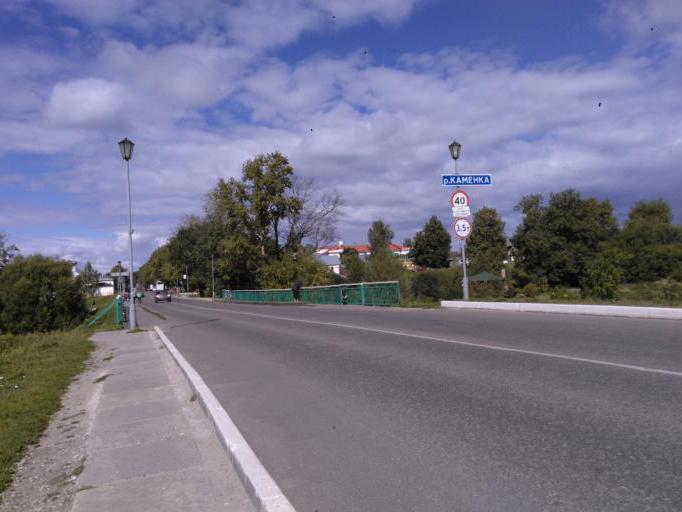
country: RU
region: Vladimir
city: Suzdal'
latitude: 56.4137
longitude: 40.4477
